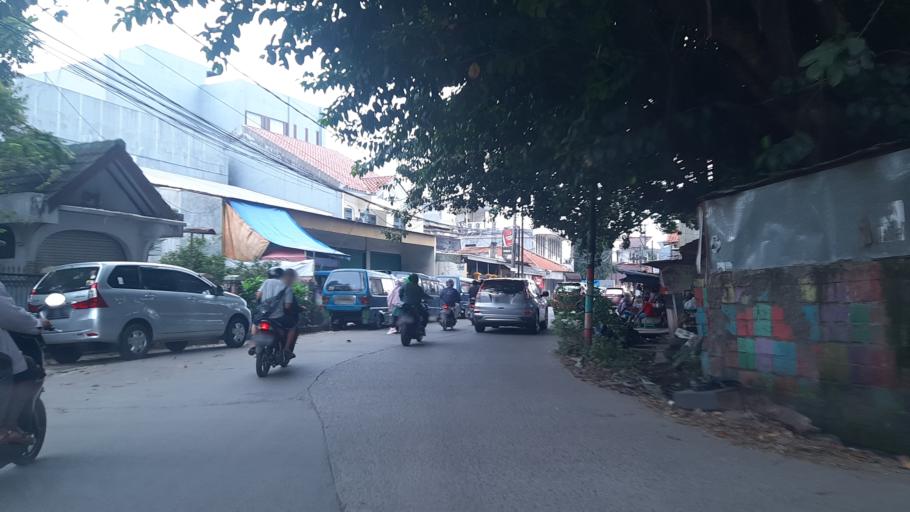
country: ID
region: West Java
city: Cibinong
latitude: -6.4694
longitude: 106.8528
